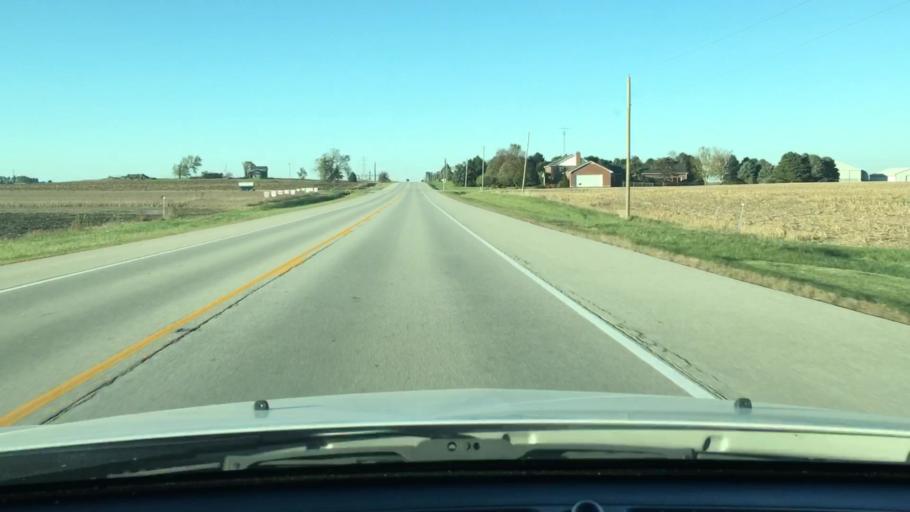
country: US
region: Illinois
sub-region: DeKalb County
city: Waterman
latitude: 41.8183
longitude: -88.7539
